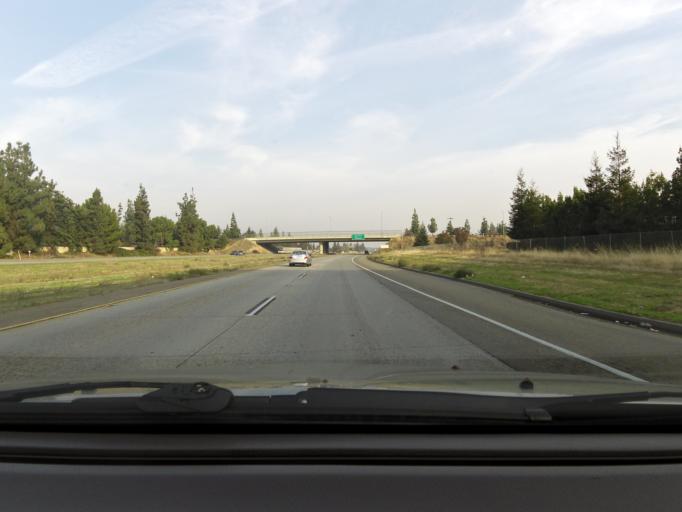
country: US
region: California
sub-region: Fresno County
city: Clovis
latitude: 36.8590
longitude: -119.7910
